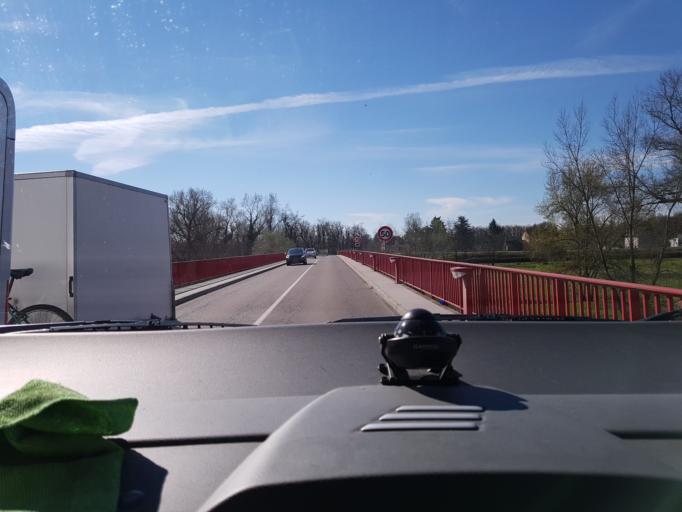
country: FR
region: Bourgogne
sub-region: Departement de Saone-et-Loire
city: Digoin
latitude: 46.4786
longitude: 3.9701
